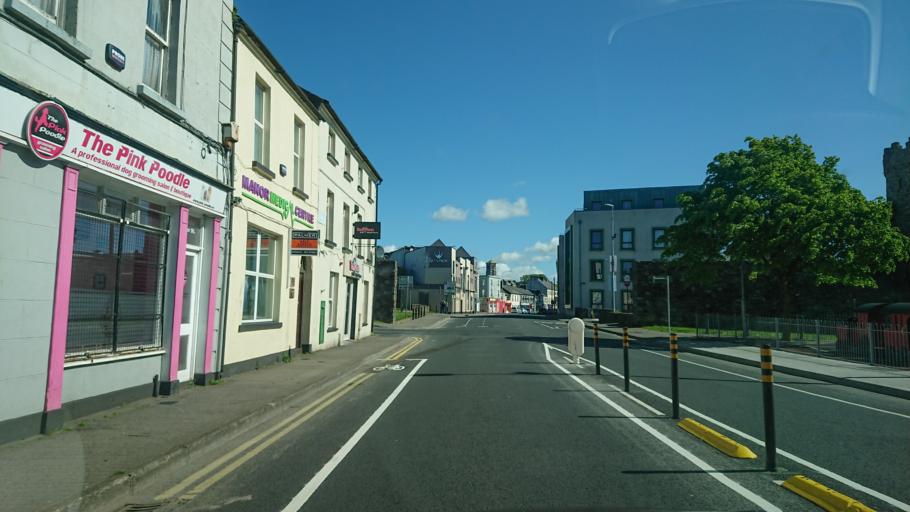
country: IE
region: Munster
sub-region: Waterford
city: Waterford
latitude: 52.2563
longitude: -7.1125
